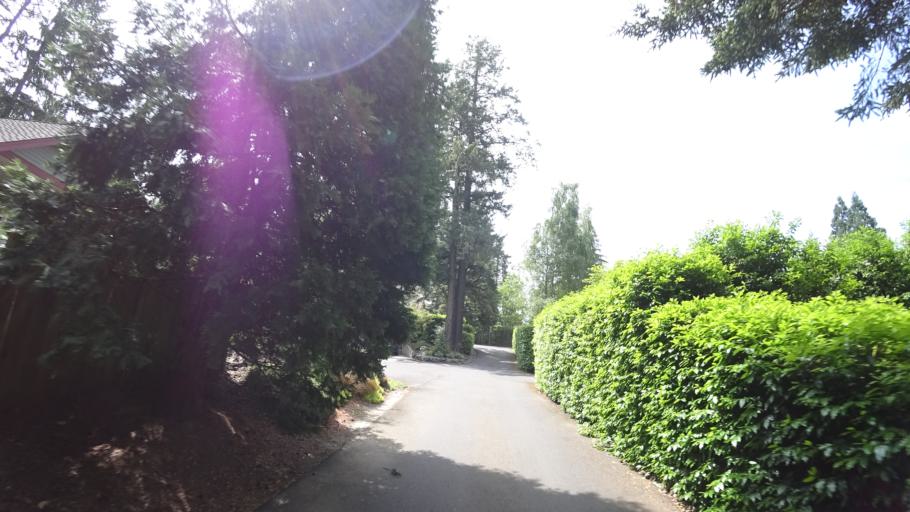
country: US
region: Oregon
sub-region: Clackamas County
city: Lake Oswego
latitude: 45.4447
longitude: -122.6682
